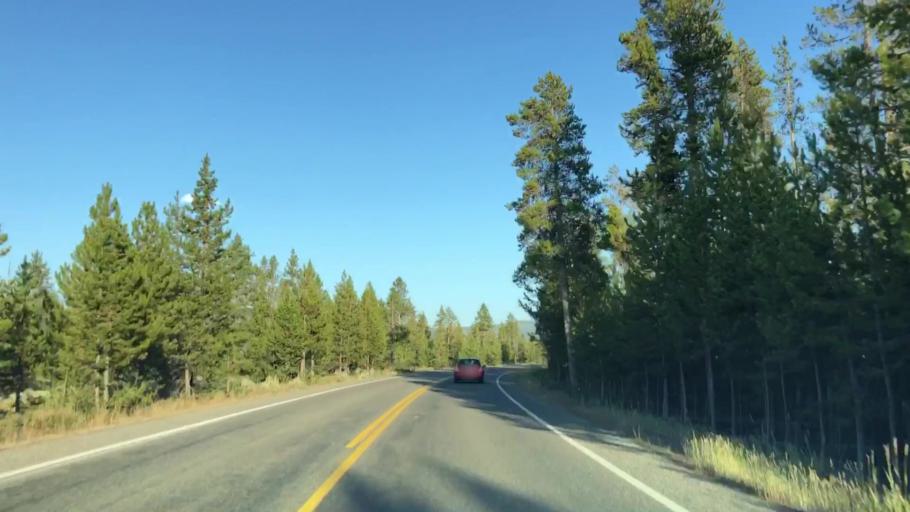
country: US
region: Montana
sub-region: Gallatin County
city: West Yellowstone
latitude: 44.6535
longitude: -111.0651
